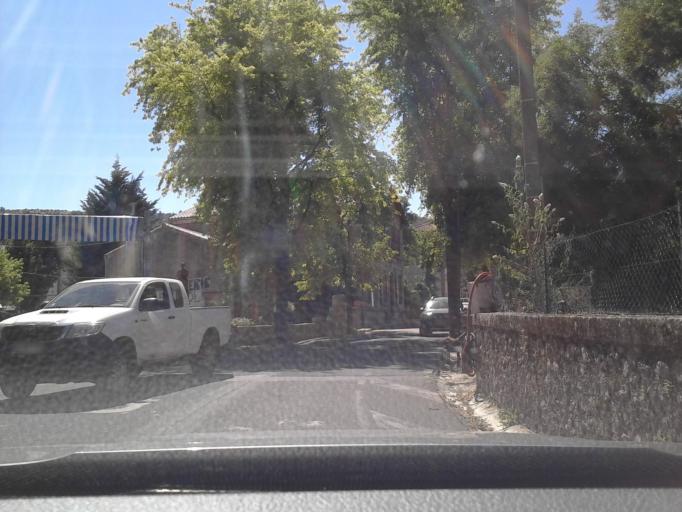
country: FR
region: Languedoc-Roussillon
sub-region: Departement de l'Herault
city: Montpeyroux
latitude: 43.7903
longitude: 3.4590
